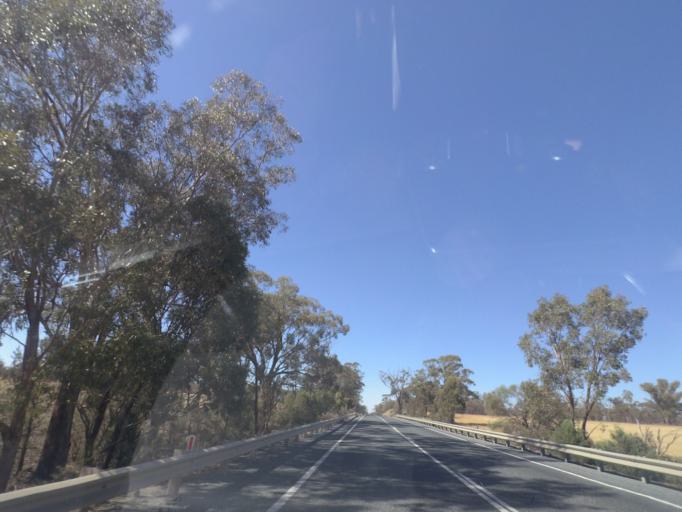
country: AU
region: New South Wales
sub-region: Bland
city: West Wyalong
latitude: -34.1650
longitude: 147.1161
